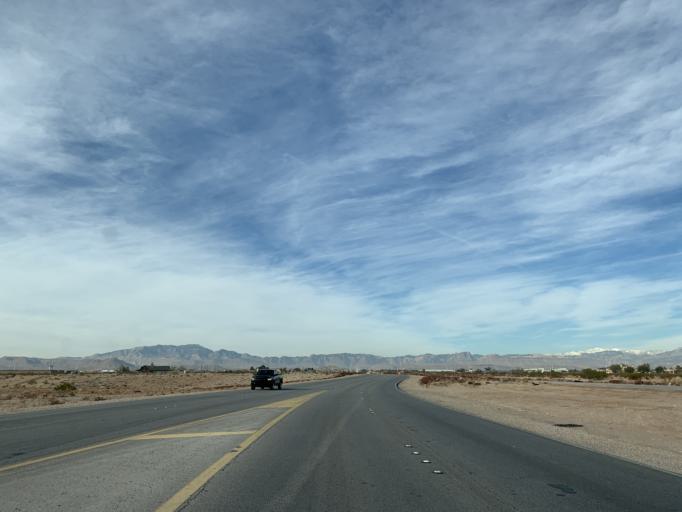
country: US
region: Nevada
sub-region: Clark County
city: Enterprise
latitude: 36.0132
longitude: -115.1855
